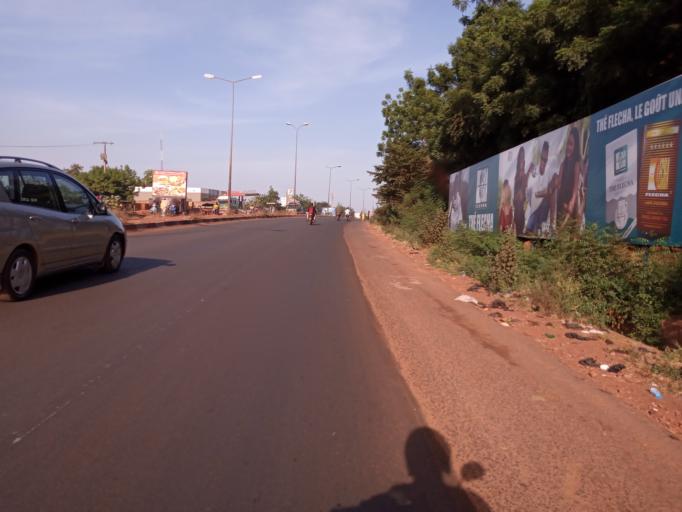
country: ML
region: Bamako
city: Bamako
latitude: 12.6170
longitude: -7.9872
